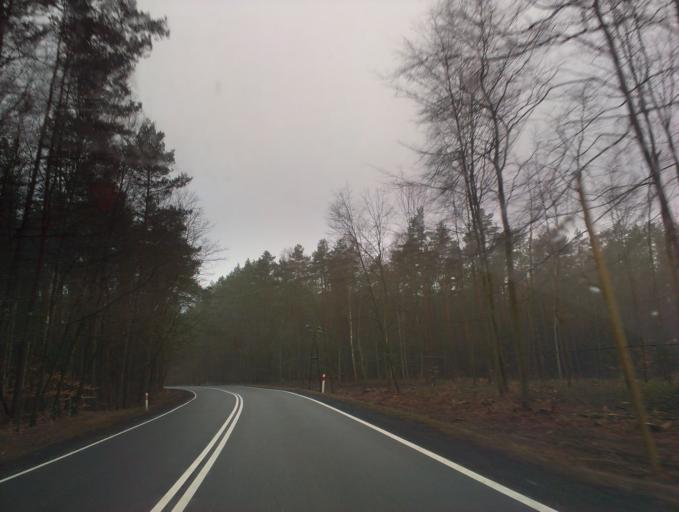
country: PL
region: Greater Poland Voivodeship
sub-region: Powiat zlotowski
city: Tarnowka
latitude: 53.2946
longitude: 16.7826
